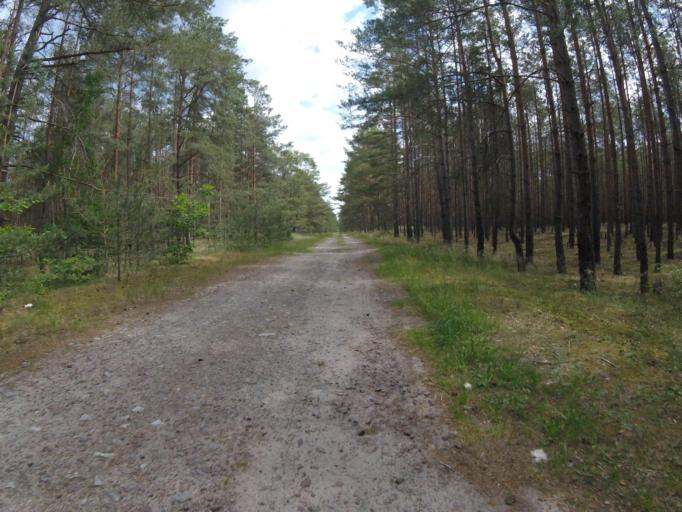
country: DE
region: Brandenburg
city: Halbe
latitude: 52.1042
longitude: 13.6851
